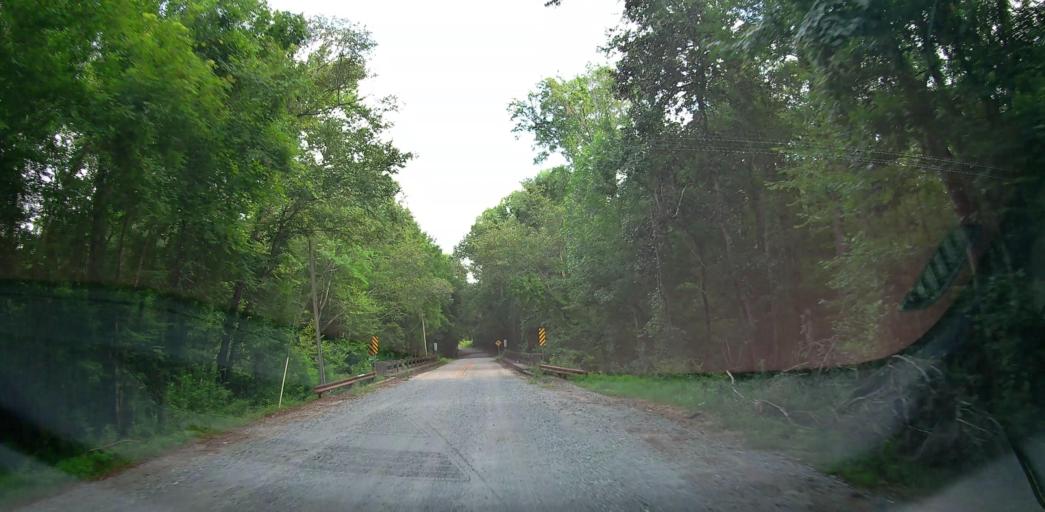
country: US
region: Georgia
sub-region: Bleckley County
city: Cochran
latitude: 32.4282
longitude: -83.4540
